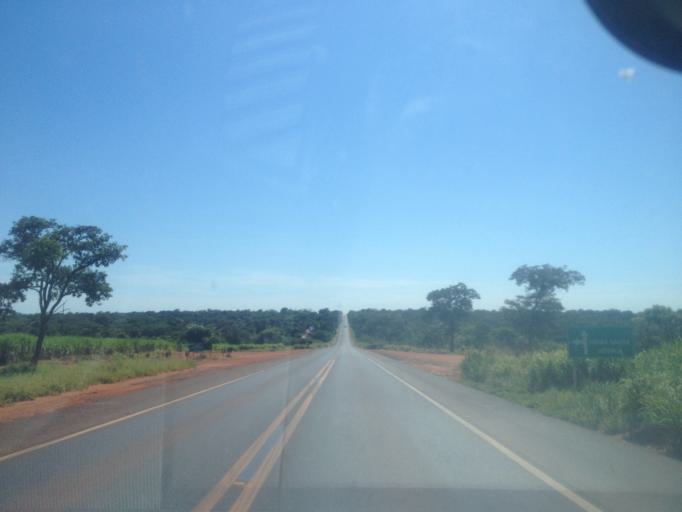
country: BR
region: Minas Gerais
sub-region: Santa Vitoria
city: Santa Vitoria
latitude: -18.8913
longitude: -50.1646
